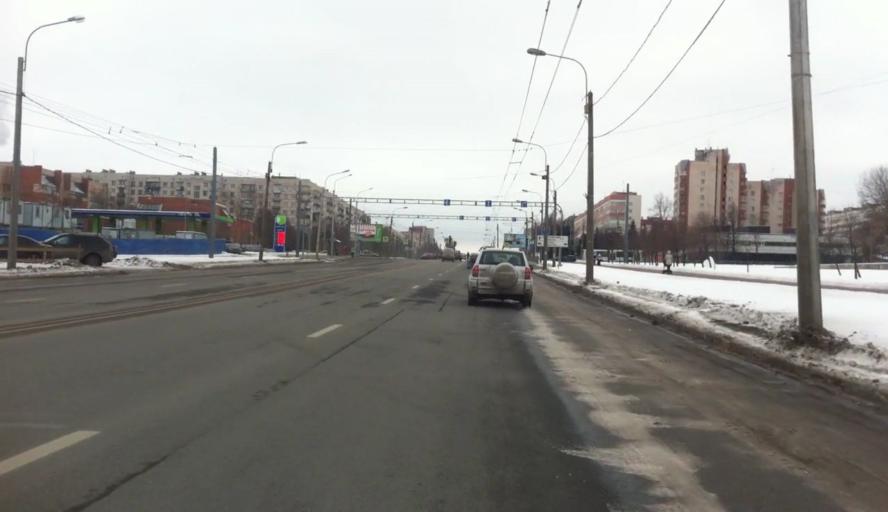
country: RU
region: St.-Petersburg
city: Uritsk
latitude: 59.8443
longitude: 30.1753
